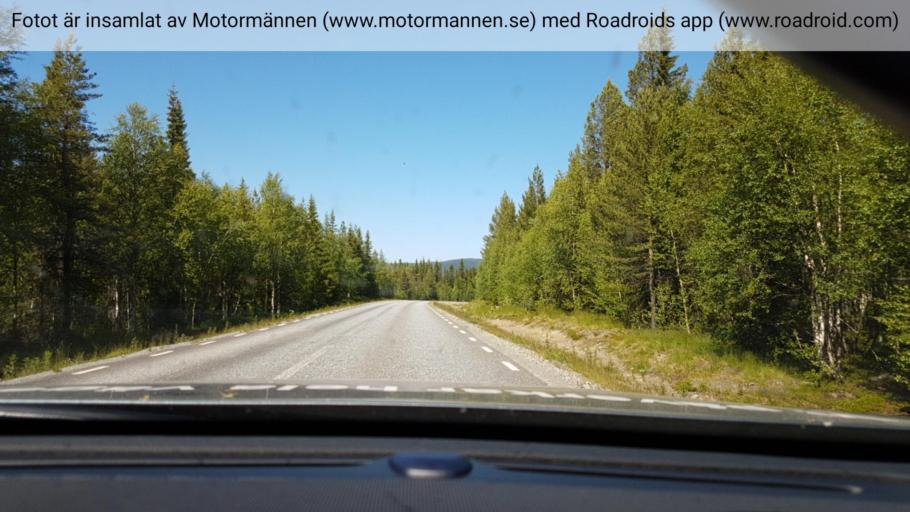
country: SE
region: Vaesterbotten
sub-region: Vilhelmina Kommun
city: Sjoberg
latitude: 64.8579
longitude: 15.8983
